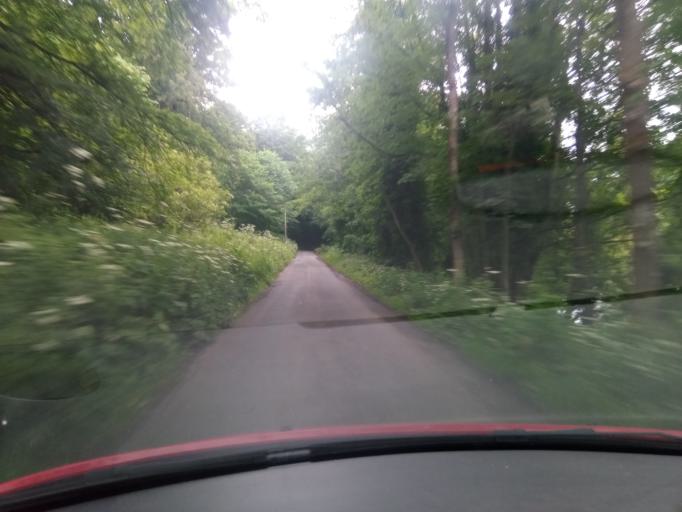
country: GB
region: Scotland
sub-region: The Scottish Borders
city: Hawick
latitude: 55.4166
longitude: -2.8173
